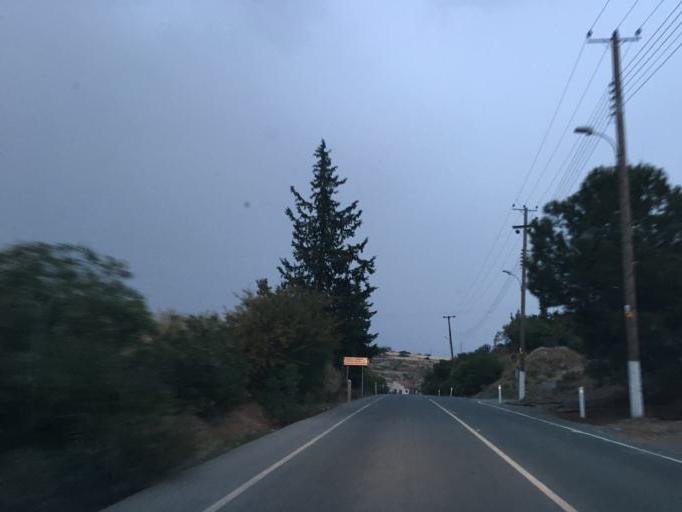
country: CY
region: Limassol
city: Parekklisha
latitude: 34.7397
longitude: 33.1587
